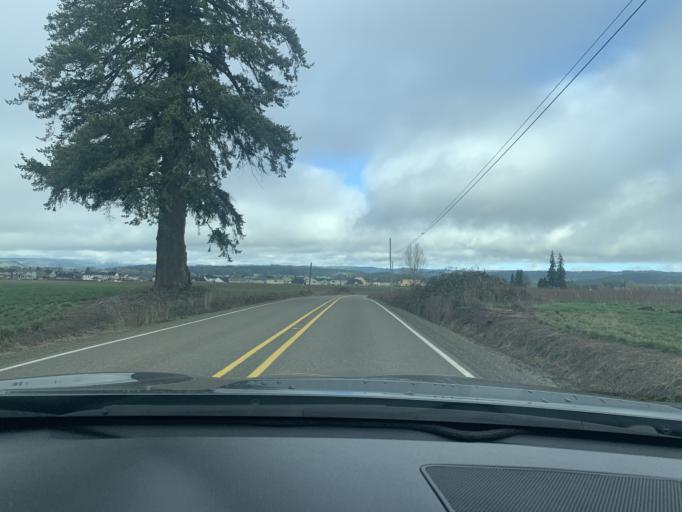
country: US
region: Oregon
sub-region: Washington County
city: North Plains
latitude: 45.5891
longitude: -122.9686
